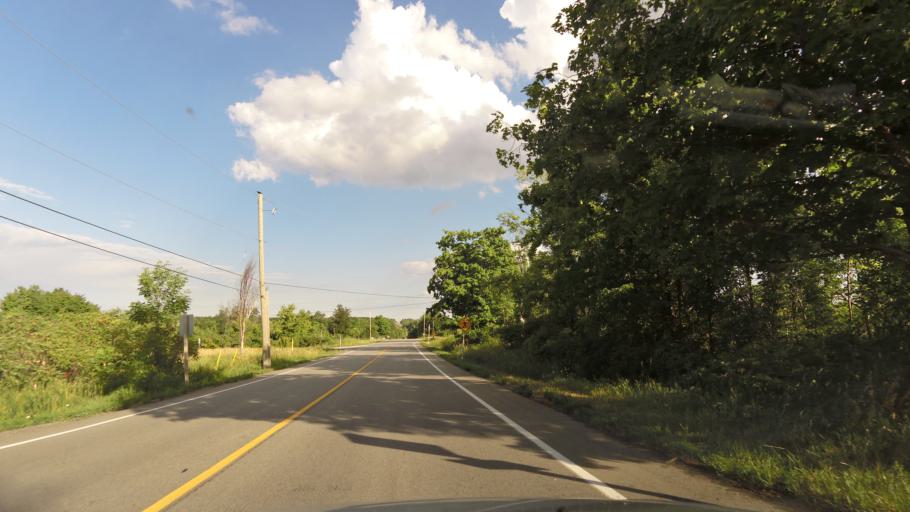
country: CA
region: Ontario
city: Brampton
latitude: 43.7428
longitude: -79.9324
